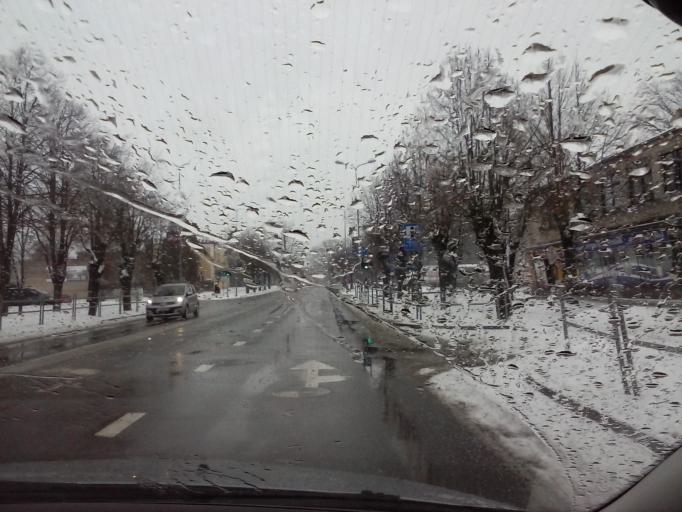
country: LV
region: Valmieras Rajons
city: Valmiera
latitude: 57.5363
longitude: 25.4067
